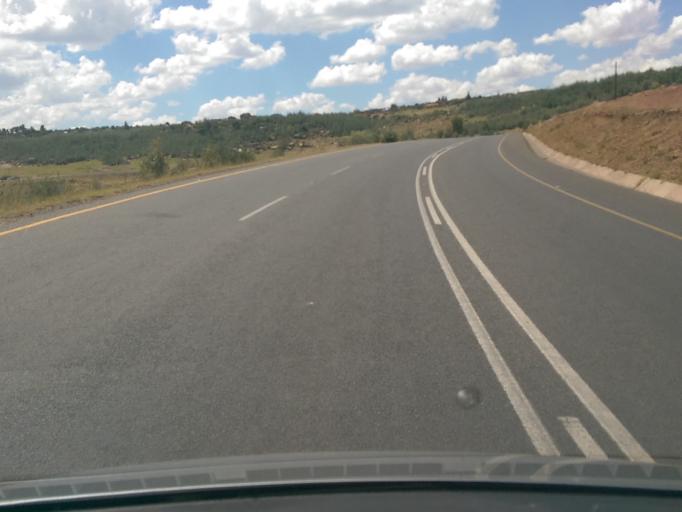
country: LS
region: Maseru
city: Maseru
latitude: -29.3985
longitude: 27.5284
